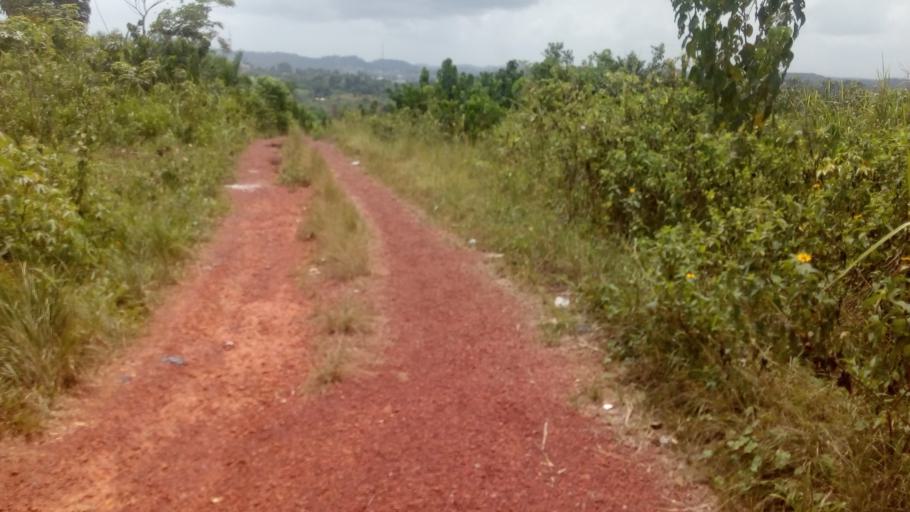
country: GH
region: Western
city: Tarkwa
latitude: 5.3020
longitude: -2.0088
